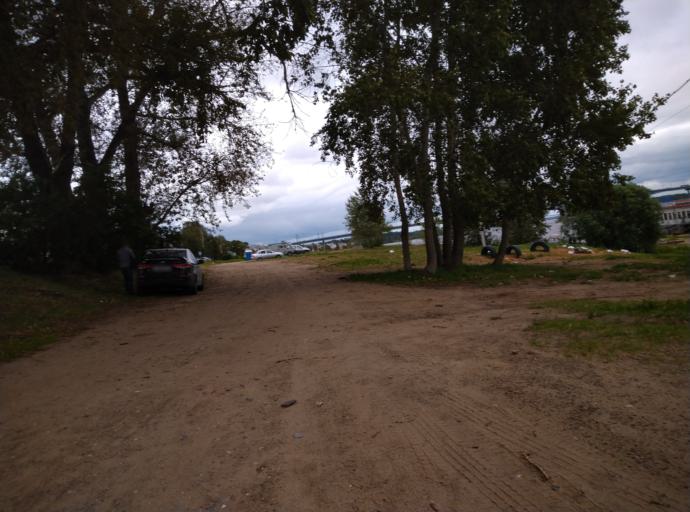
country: RU
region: Kostroma
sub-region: Kostromskoy Rayon
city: Kostroma
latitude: 57.7597
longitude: 40.9337
